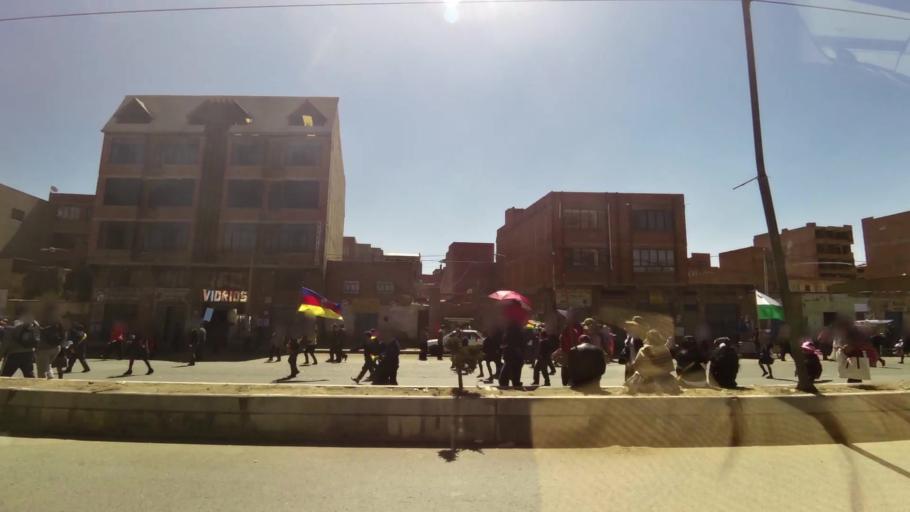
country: BO
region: La Paz
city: La Paz
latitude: -16.4934
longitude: -68.1962
